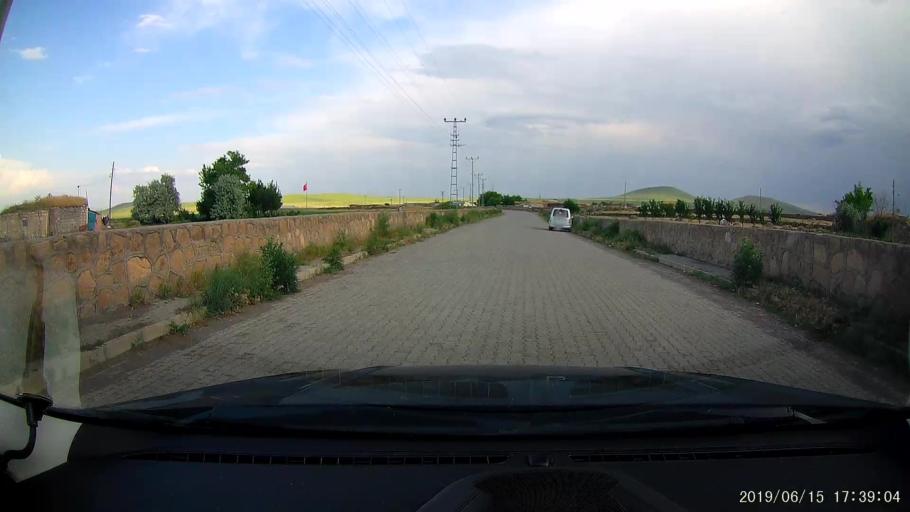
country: TR
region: Kars
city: Basgedikler
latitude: 40.5180
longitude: 43.5690
